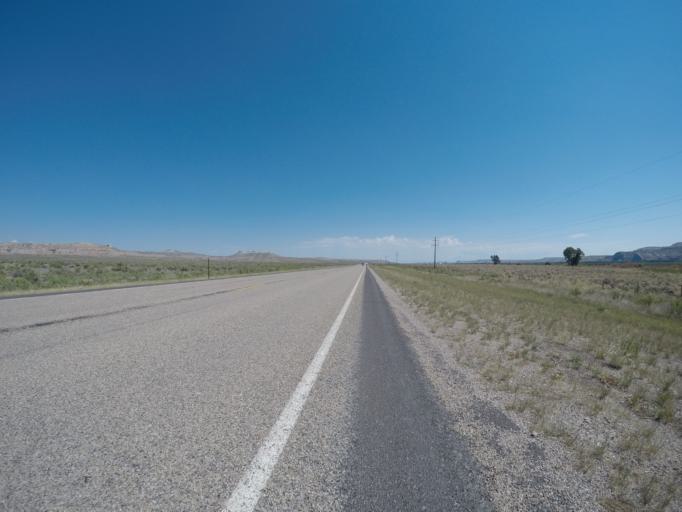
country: US
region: Wyoming
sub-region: Sublette County
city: Marbleton
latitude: 42.3445
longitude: -110.1631
